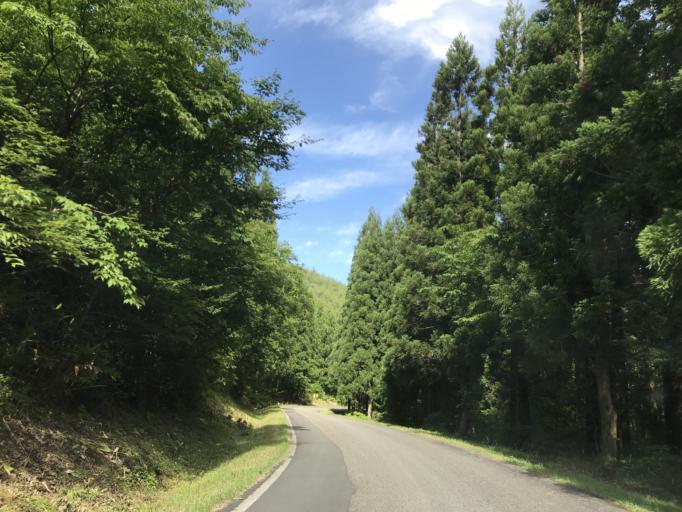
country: JP
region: Iwate
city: Ichinoseki
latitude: 38.9267
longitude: 140.9321
